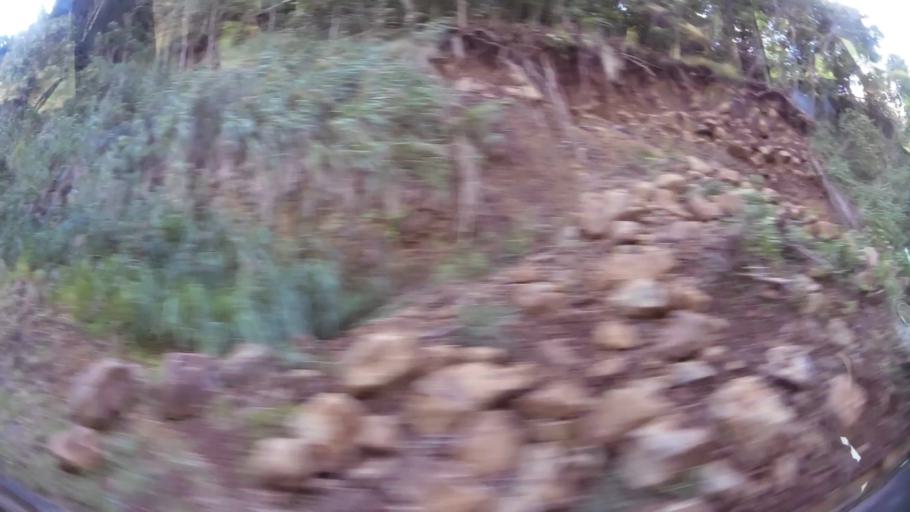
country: DM
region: Saint Paul
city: Mahaut
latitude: 15.3412
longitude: -61.3804
